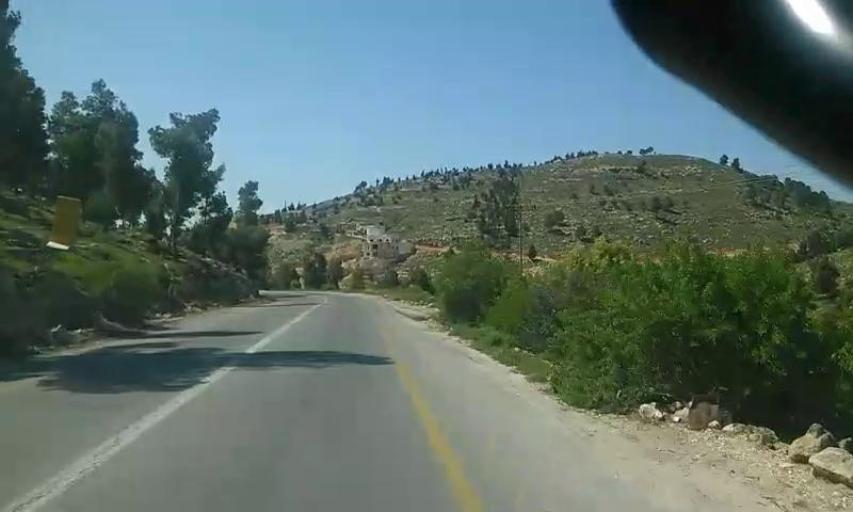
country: PS
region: West Bank
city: Ar Rihiyah
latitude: 31.4909
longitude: 35.0669
